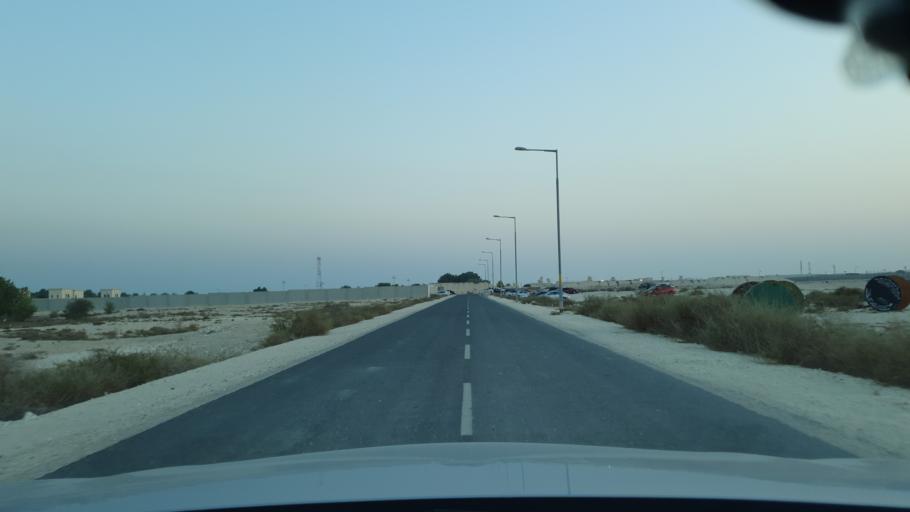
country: BH
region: Central Governorate
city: Dar Kulayb
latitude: 25.9577
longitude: 50.6113
